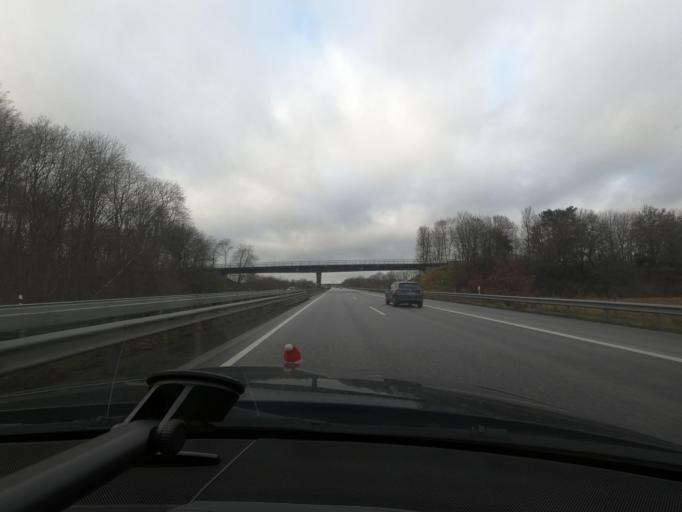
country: DE
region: Schleswig-Holstein
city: Bokel
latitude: 54.2493
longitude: 9.8114
